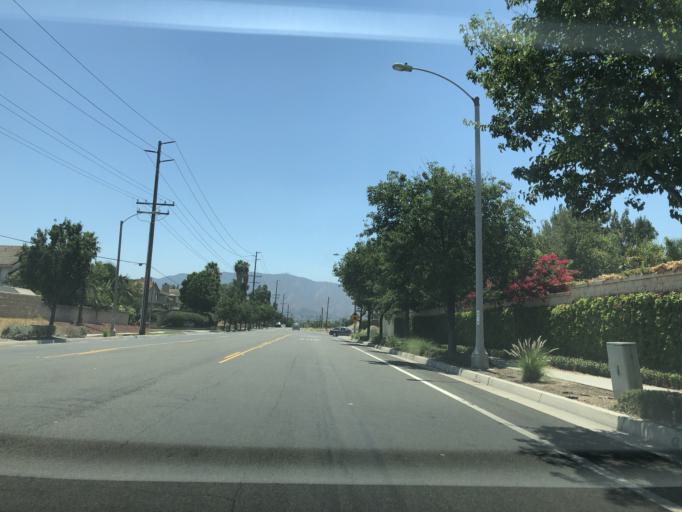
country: US
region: California
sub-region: Riverside County
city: Corona
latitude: 33.9100
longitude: -117.5942
